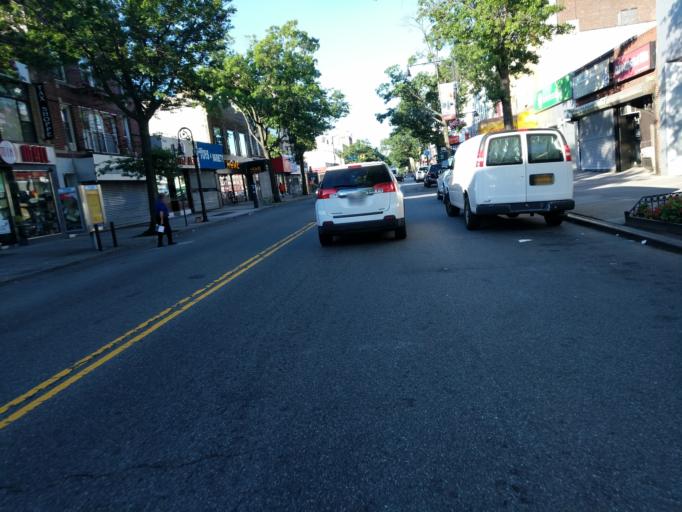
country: US
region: New York
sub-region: Queens County
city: Long Island City
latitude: 40.7647
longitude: -73.9144
